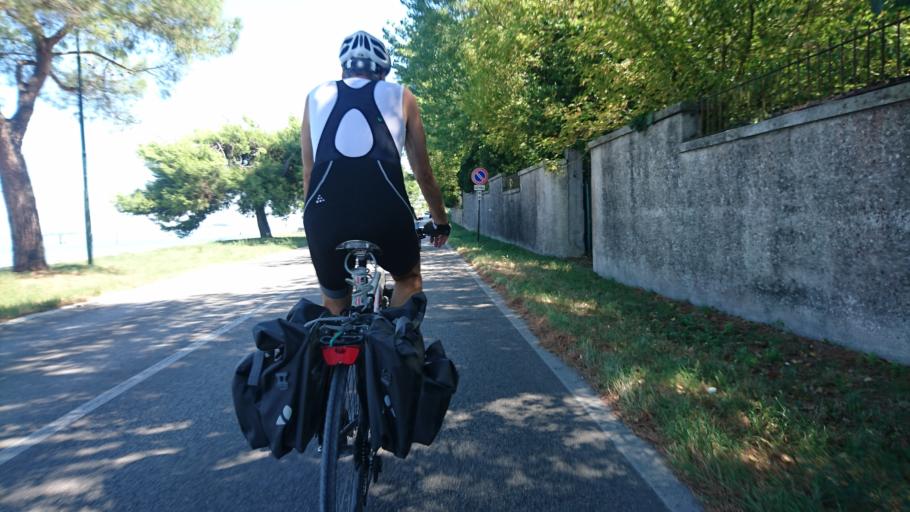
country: IT
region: Veneto
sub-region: Provincia di Venezia
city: San Pietro in Volta
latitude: 45.3537
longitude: 12.3257
